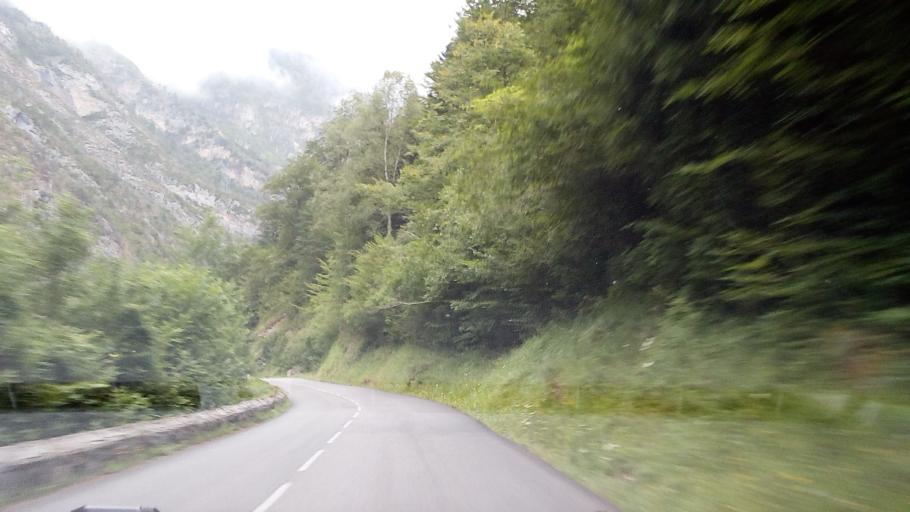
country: FR
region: Aquitaine
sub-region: Departement des Pyrenees-Atlantiques
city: Laruns
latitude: 42.9596
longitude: -0.4399
